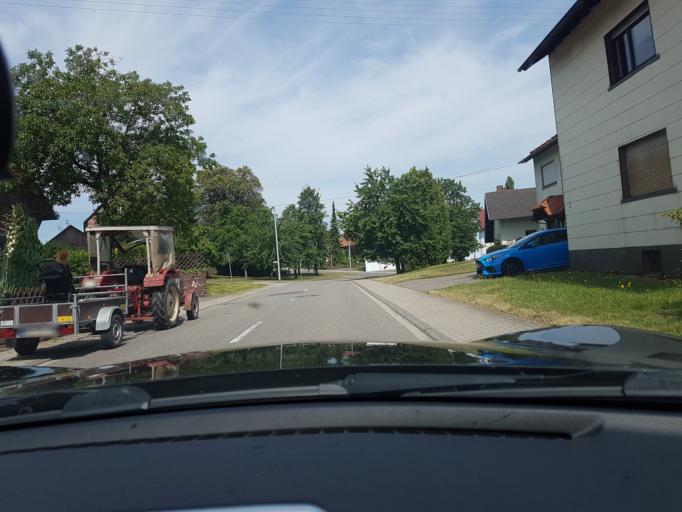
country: DE
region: Baden-Wuerttemberg
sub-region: Karlsruhe Region
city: Mudau
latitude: 49.5383
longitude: 9.1510
